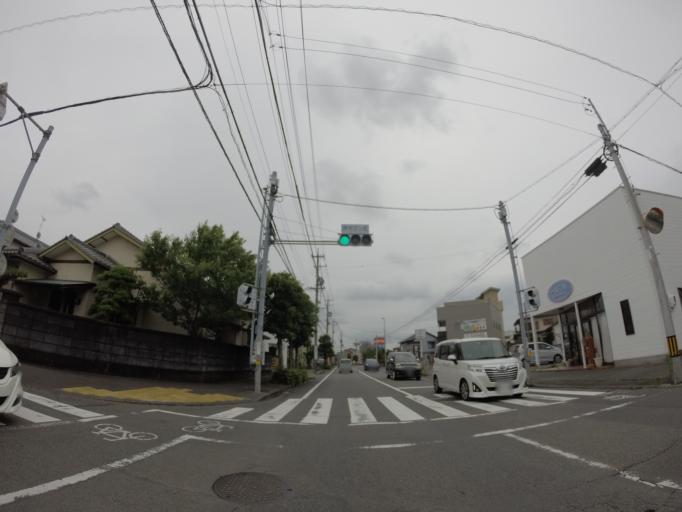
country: JP
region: Shizuoka
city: Fujieda
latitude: 34.8518
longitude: 138.2491
